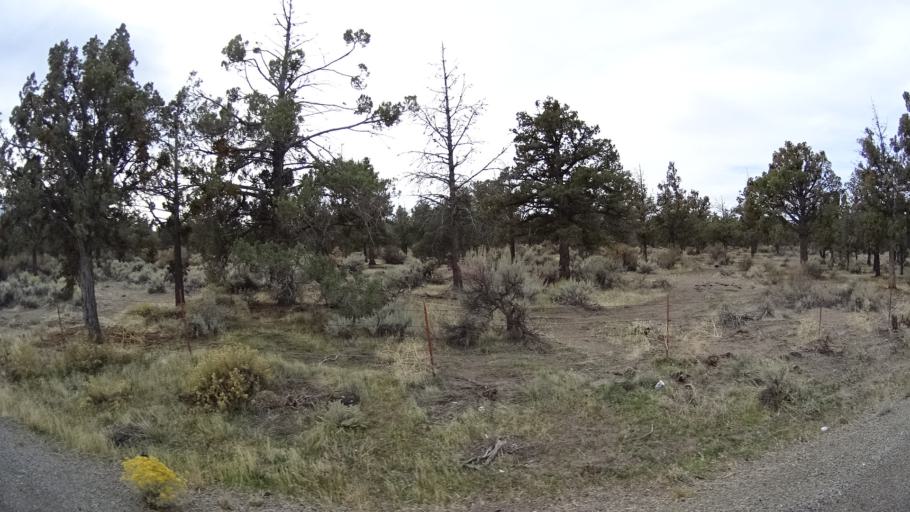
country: US
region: California
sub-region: Siskiyou County
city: Weed
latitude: 41.5853
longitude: -122.2965
